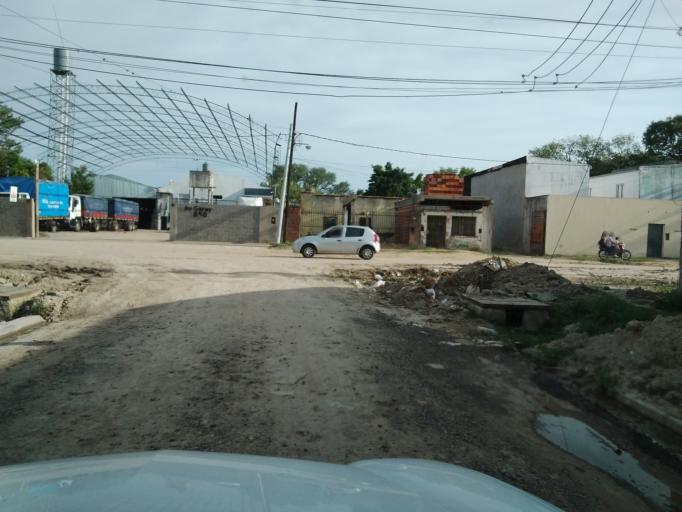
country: AR
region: Corrientes
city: Corrientes
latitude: -27.4928
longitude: -58.8433
